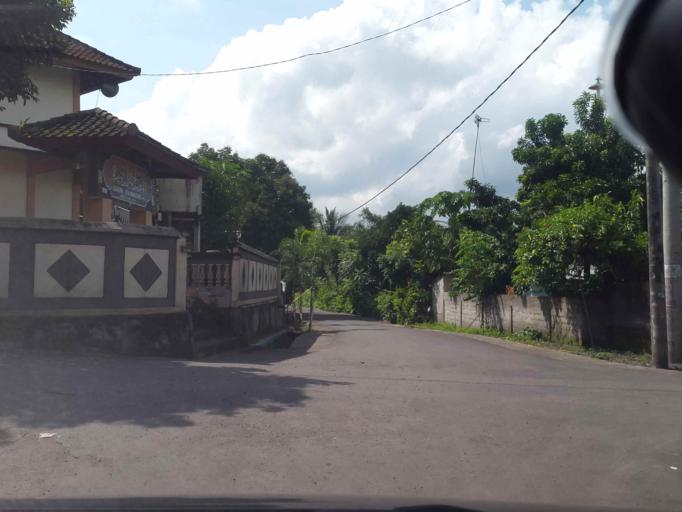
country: ID
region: West Nusa Tenggara
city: Selat
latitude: -8.5633
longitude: 116.2082
